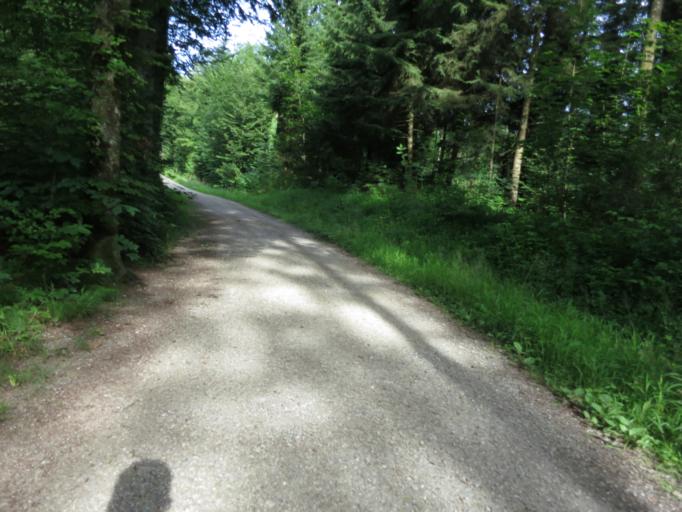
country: CH
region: Zurich
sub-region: Bezirk Hinwil
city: Rueti / Westlicher Dorfteil
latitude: 47.2564
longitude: 8.8317
